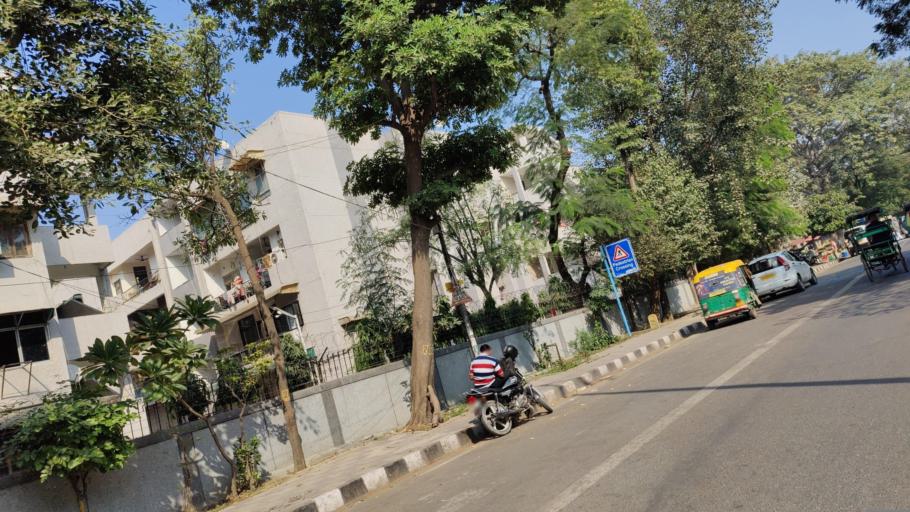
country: IN
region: NCT
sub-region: North West Delhi
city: Pitampura
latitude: 28.7101
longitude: 77.1261
